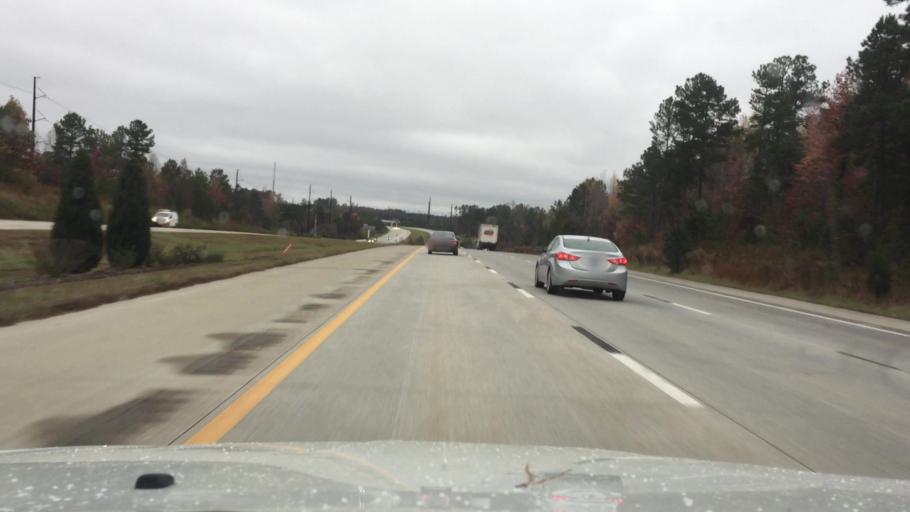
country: US
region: North Carolina
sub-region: Wake County
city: Green Level
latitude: 35.8108
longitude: -78.8921
